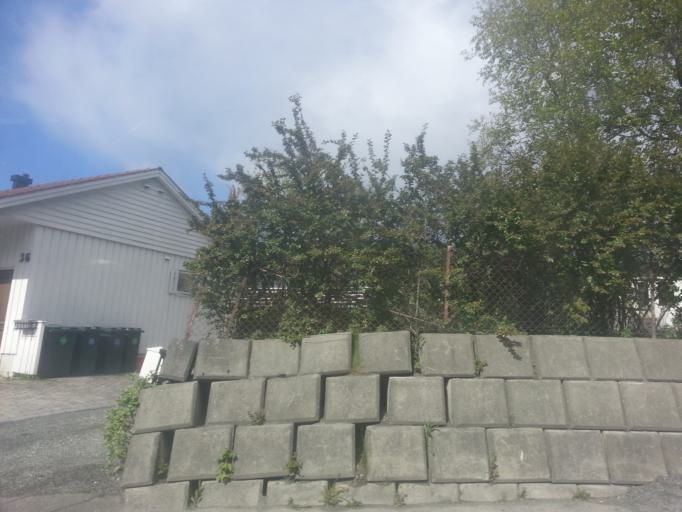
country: NO
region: Sor-Trondelag
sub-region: Trondheim
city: Trondheim
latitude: 63.4162
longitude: 10.4289
